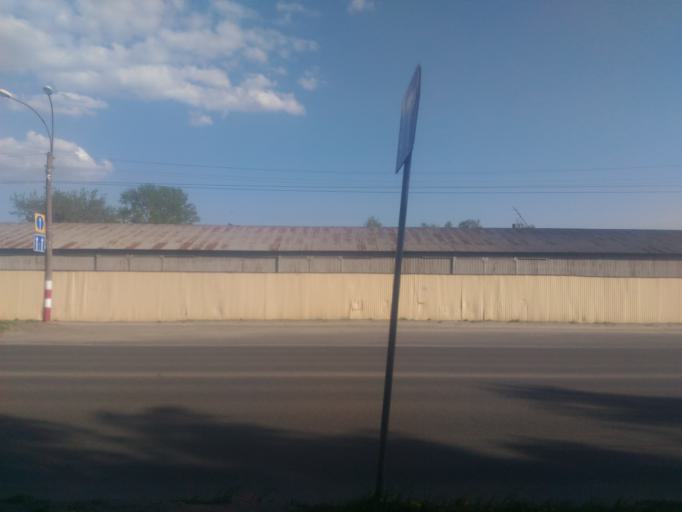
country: RU
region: Ulyanovsk
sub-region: Ulyanovskiy Rayon
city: Ulyanovsk
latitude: 54.2854
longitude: 48.3573
